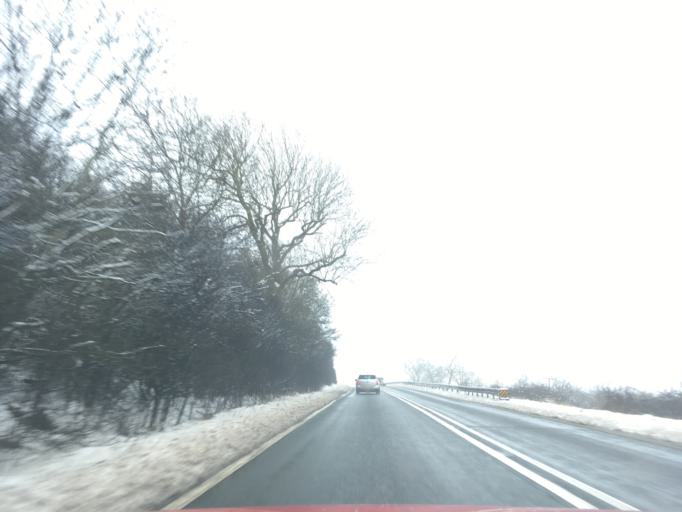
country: GB
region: England
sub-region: Warwickshire
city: Stratford-upon-Avon
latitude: 52.2004
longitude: -1.7714
